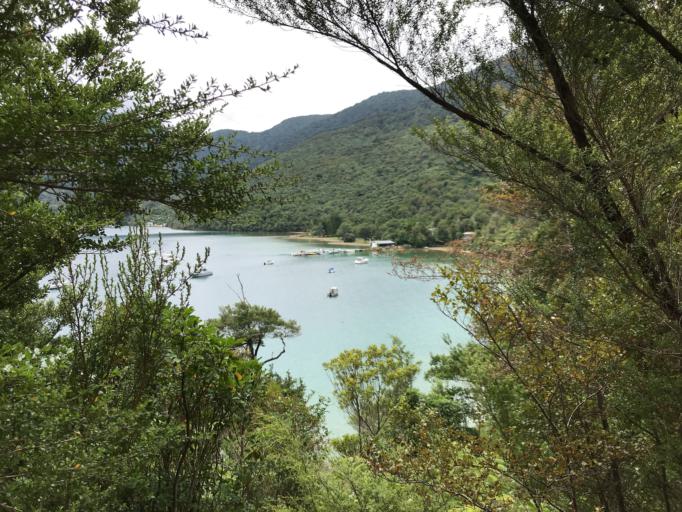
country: NZ
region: Marlborough
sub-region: Marlborough District
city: Picton
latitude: -41.0975
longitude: 174.1874
